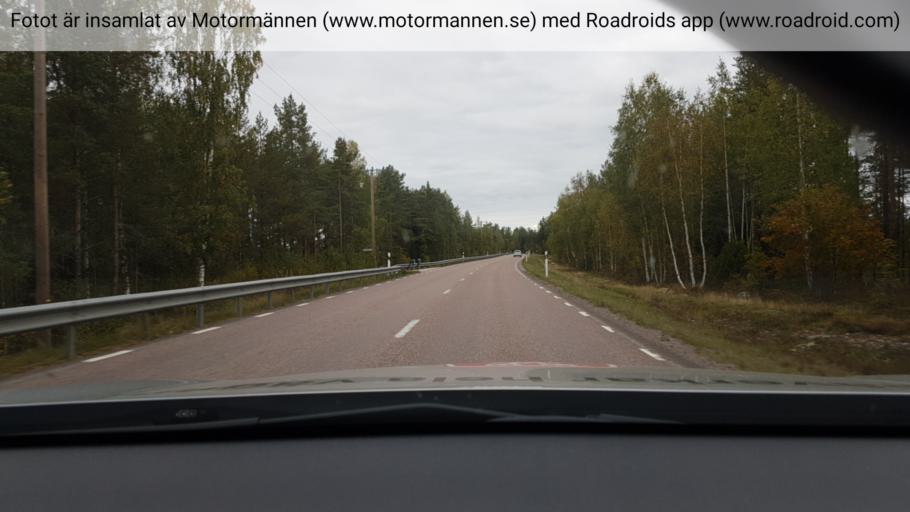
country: SE
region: Gaevleborg
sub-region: Gavle Kommun
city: Valbo
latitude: 60.5642
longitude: 16.9538
